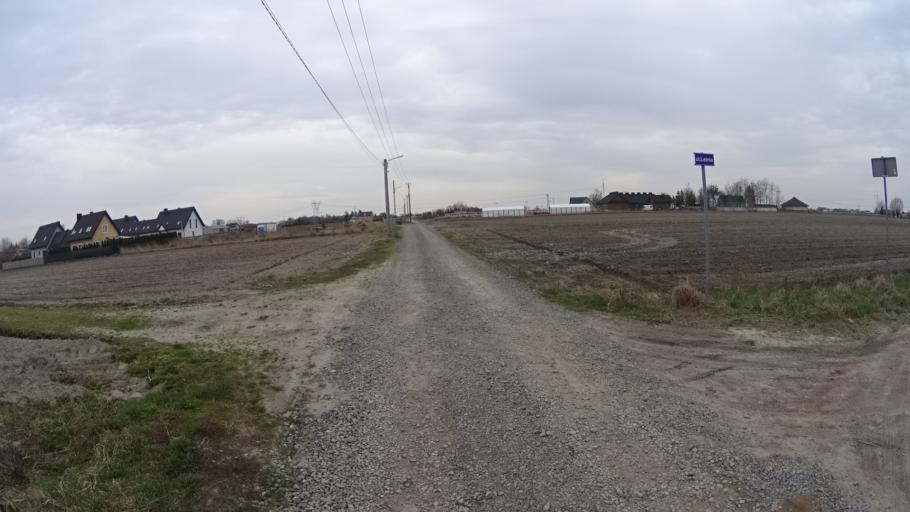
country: PL
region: Masovian Voivodeship
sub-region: Powiat warszawski zachodni
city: Jozefow
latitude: 52.2444
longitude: 20.6885
